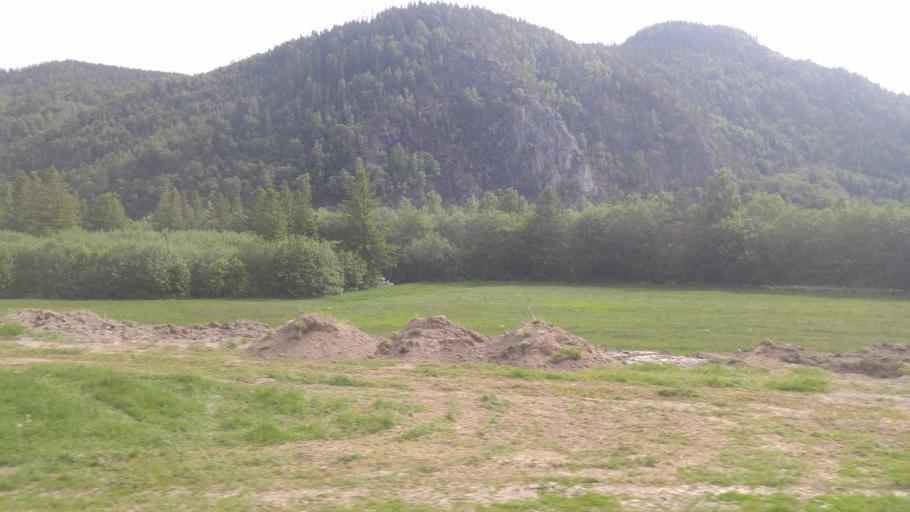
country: NO
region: Sor-Trondelag
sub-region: Midtre Gauldal
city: Storen
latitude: 63.0757
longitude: 10.2543
